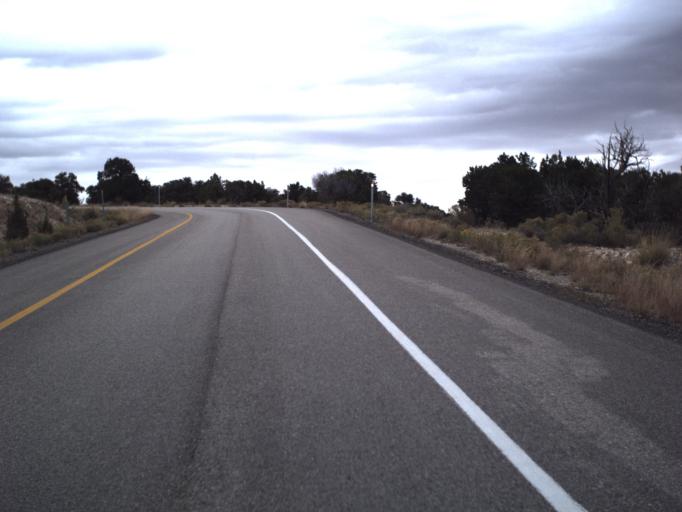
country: US
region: Utah
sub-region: Emery County
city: Ferron
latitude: 38.8497
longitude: -110.9272
